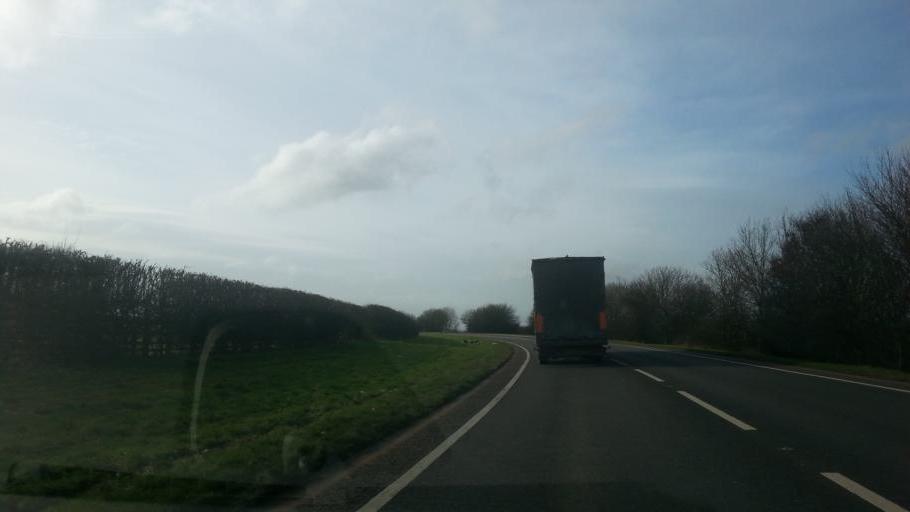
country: GB
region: England
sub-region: District of Rutland
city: Ridlington
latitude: 52.6006
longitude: -0.7513
